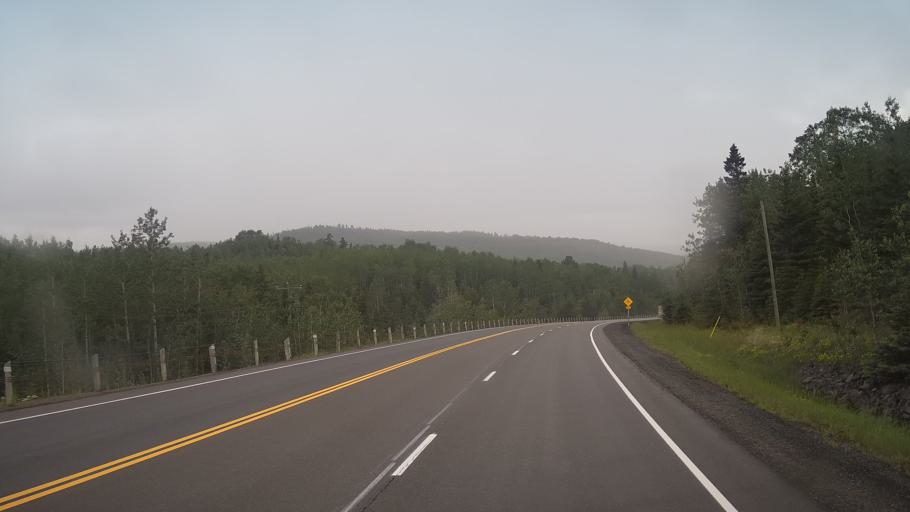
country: CA
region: Ontario
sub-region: Thunder Bay District
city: Thunder Bay
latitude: 48.5325
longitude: -89.6125
